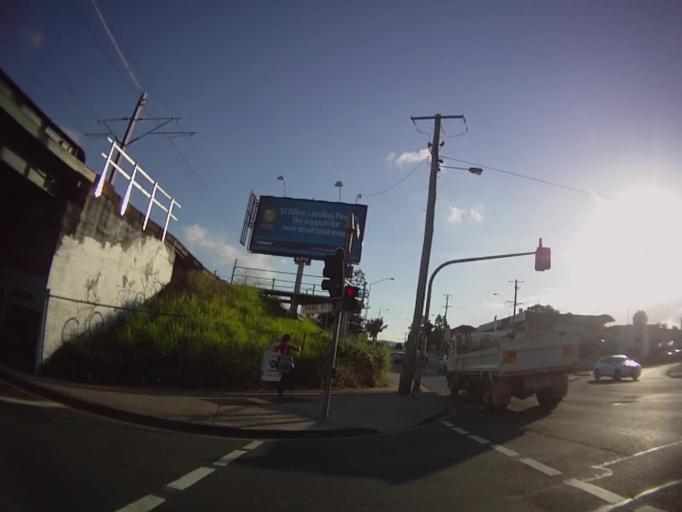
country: AU
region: Queensland
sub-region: Brisbane
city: Milton
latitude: -27.4692
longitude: 153.0039
